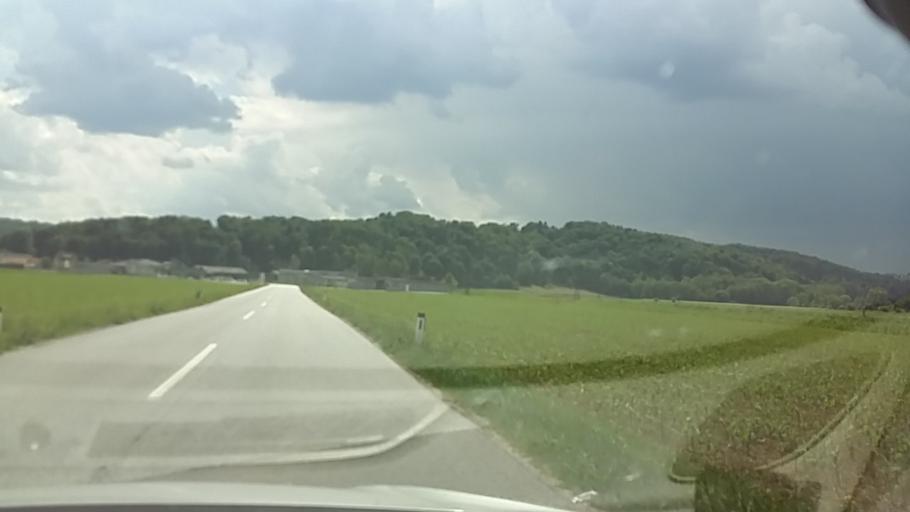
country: AT
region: Styria
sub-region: Politischer Bezirk Suedoststeiermark
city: Breitenfeld an der Rittschein
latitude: 47.0388
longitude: 15.9626
